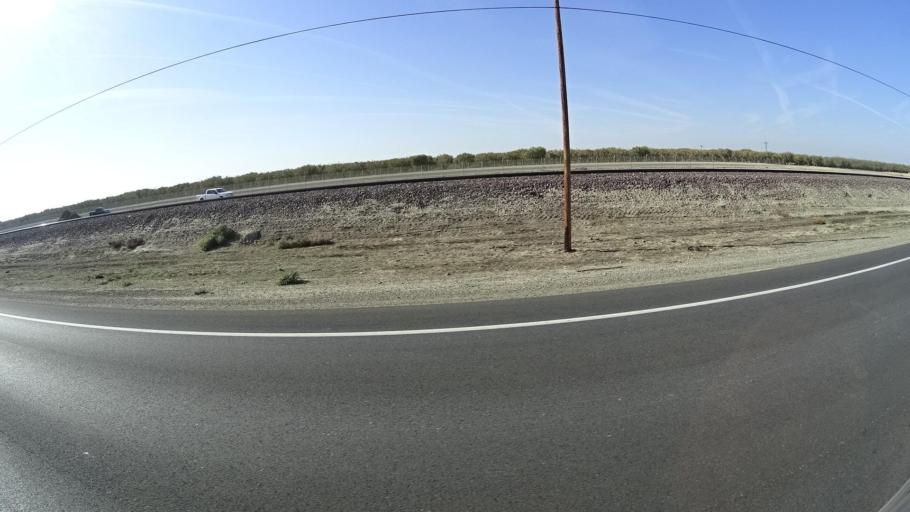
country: US
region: California
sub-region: Kern County
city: Wasco
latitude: 35.6508
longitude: -119.3309
